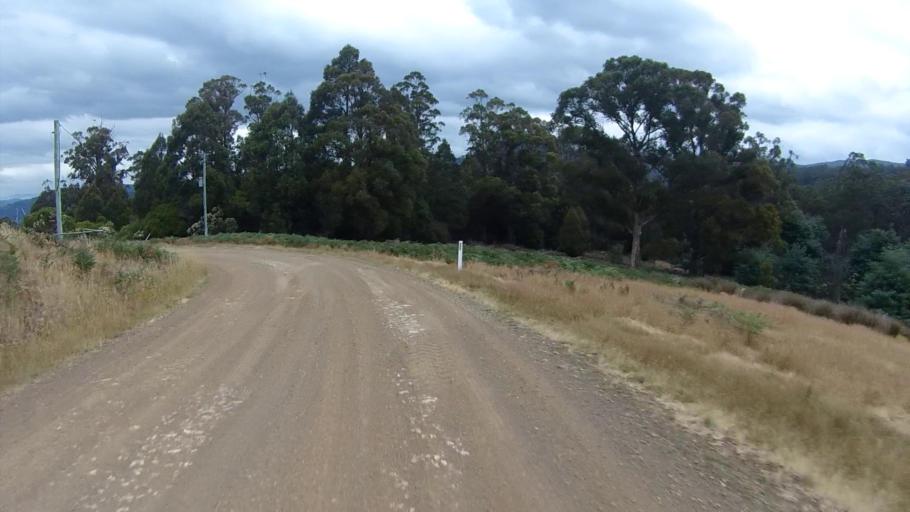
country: AU
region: Tasmania
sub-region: Huon Valley
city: Huonville
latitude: -42.9581
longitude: 147.0500
